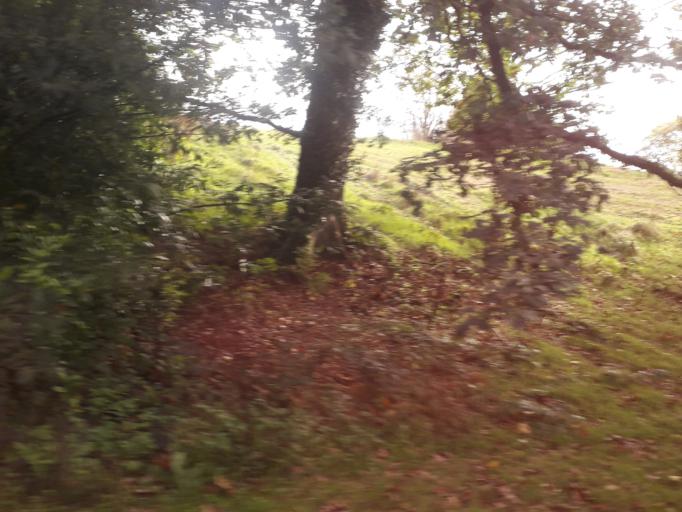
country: IE
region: Leinster
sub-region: Laois
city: Mountrath
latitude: 53.0284
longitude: -7.5240
